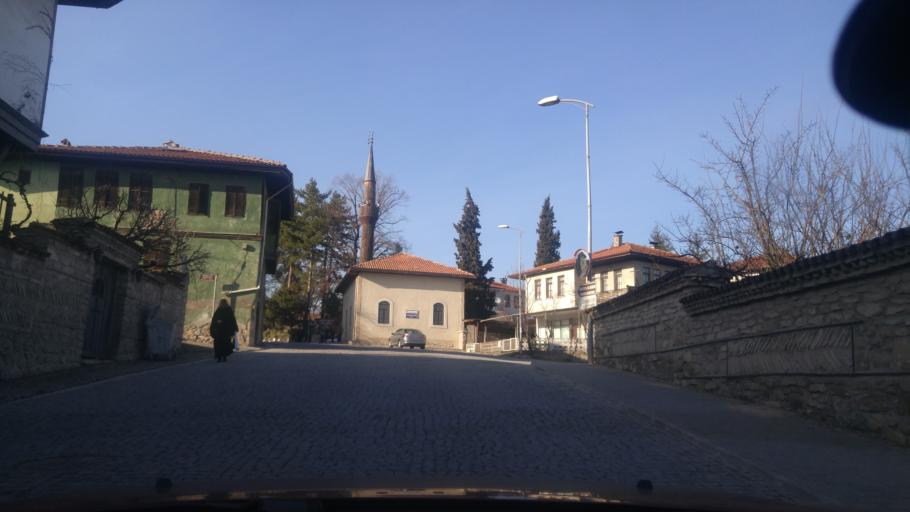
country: TR
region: Karabuk
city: Safranbolu
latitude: 41.2619
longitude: 32.6747
